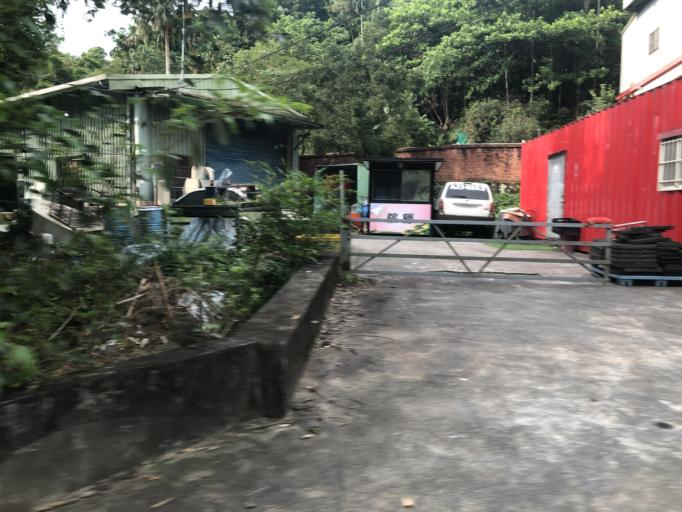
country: TW
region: Taiwan
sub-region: Taoyuan
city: Taoyuan
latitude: 24.9215
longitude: 121.3827
